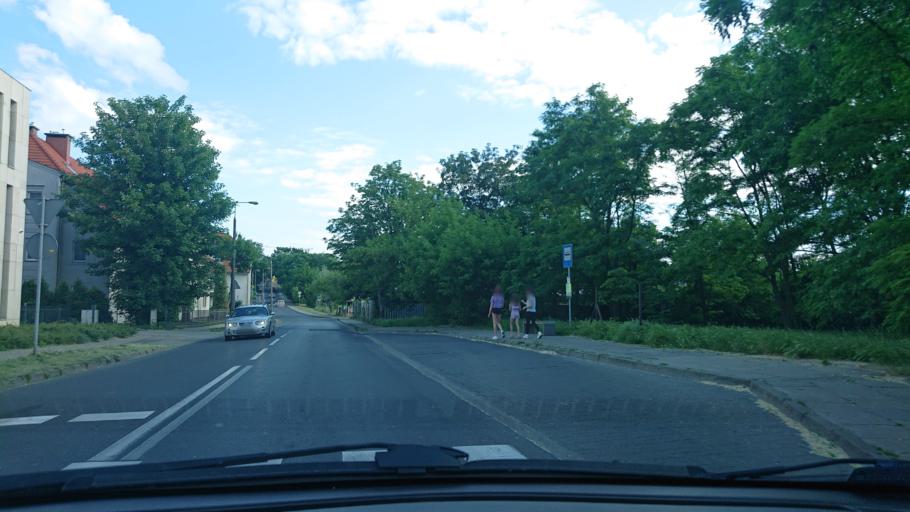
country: PL
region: Greater Poland Voivodeship
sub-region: Powiat gnieznienski
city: Gniezno
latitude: 52.5348
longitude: 17.5915
